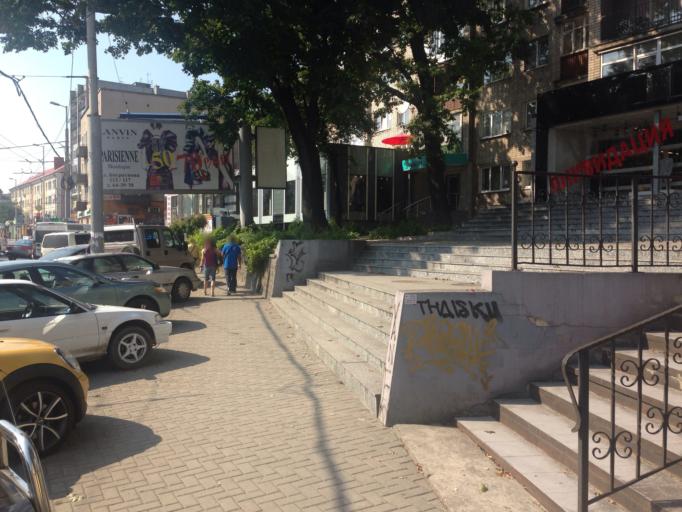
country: RU
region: Kaliningrad
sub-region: Gorod Kaliningrad
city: Kaliningrad
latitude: 54.7209
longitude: 20.4838
